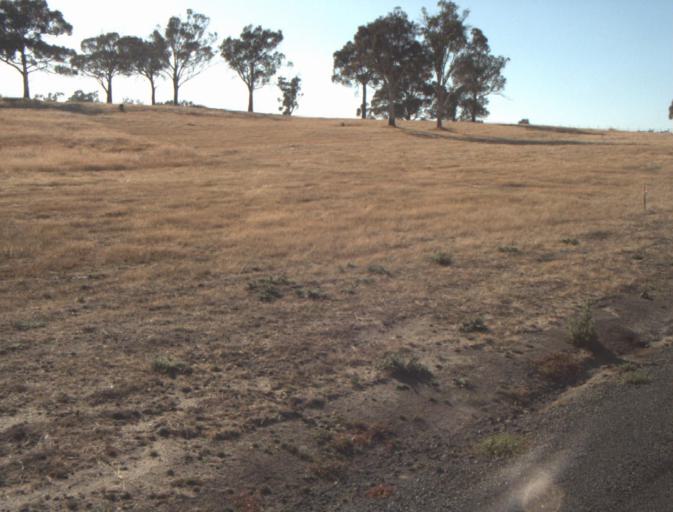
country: AU
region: Tasmania
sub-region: Launceston
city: Newstead
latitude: -41.4369
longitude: 147.2252
